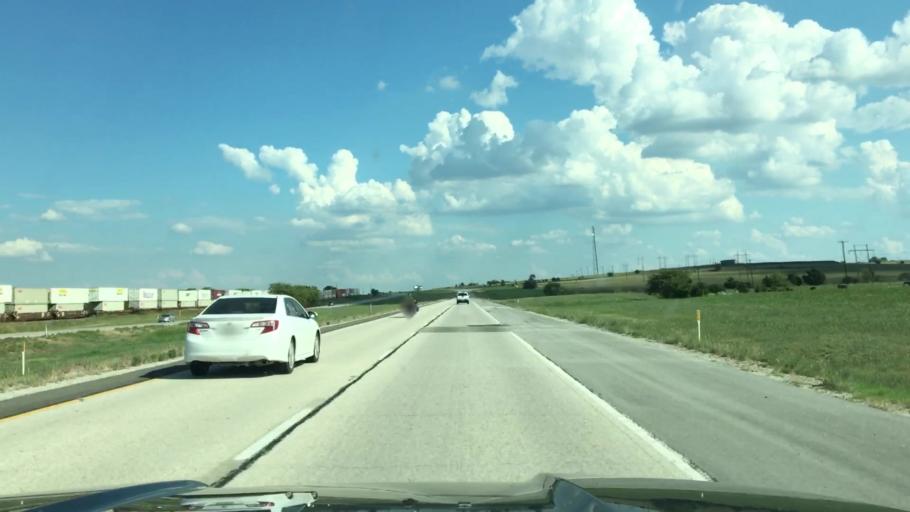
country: US
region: Texas
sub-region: Wise County
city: Boyd
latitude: 33.1617
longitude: -97.5266
